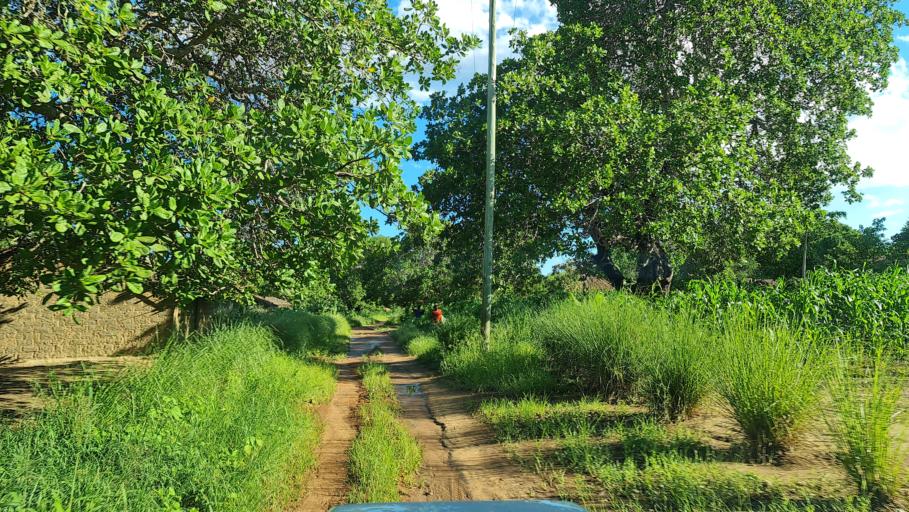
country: MZ
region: Nampula
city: Ilha de Mocambique
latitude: -14.9276
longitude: 40.2200
